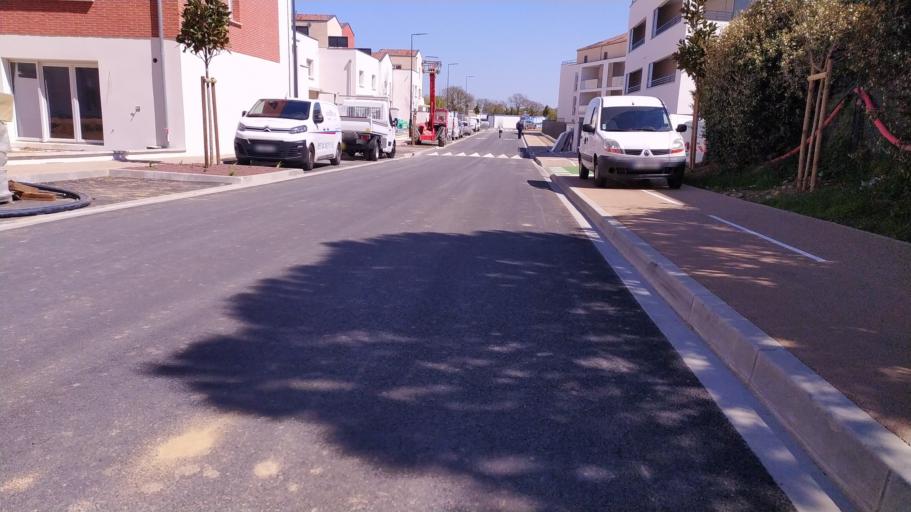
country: FR
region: Midi-Pyrenees
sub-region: Departement de la Haute-Garonne
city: Plaisance-du-Touch
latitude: 43.5697
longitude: 1.3119
